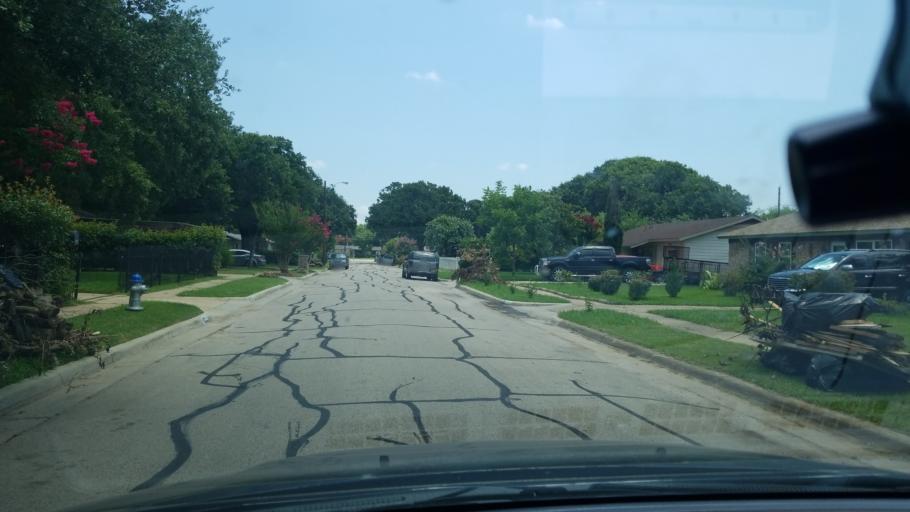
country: US
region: Texas
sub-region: Dallas County
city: Balch Springs
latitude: 32.7149
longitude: -96.6507
